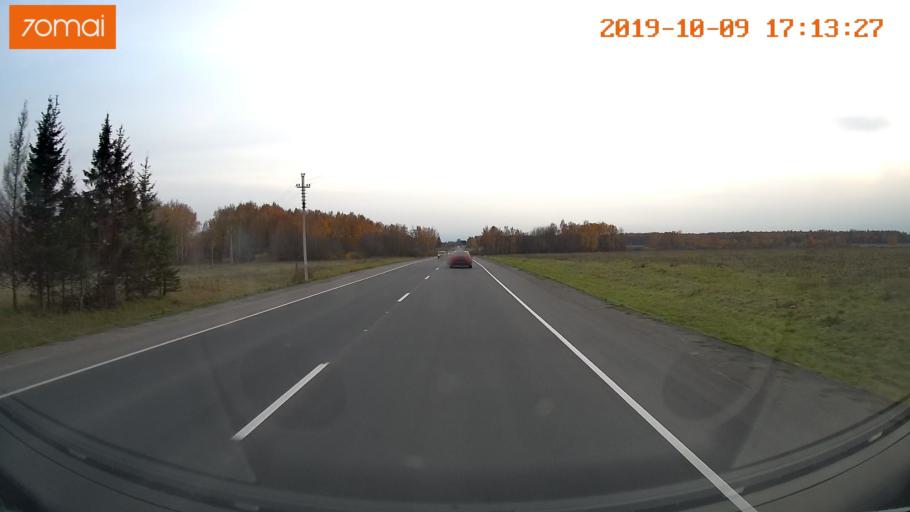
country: RU
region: Ivanovo
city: Privolzhsk
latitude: 57.3152
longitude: 41.2240
